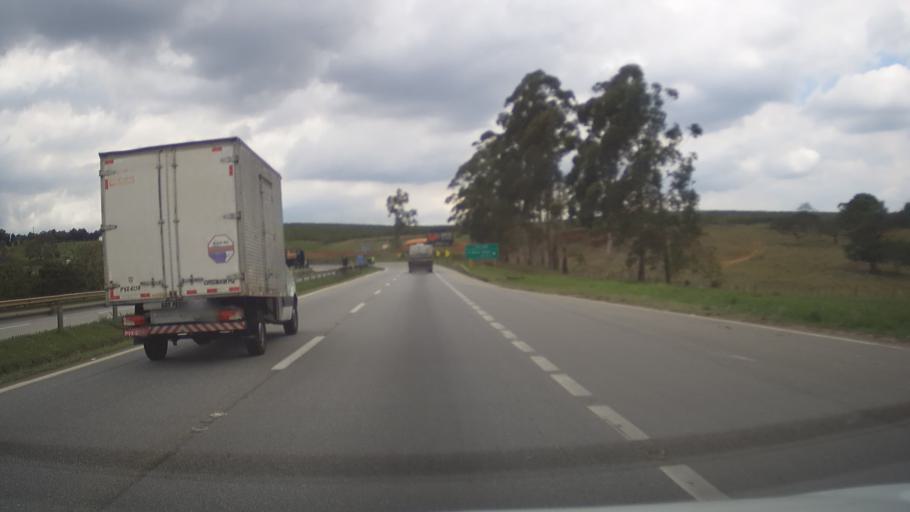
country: BR
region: Minas Gerais
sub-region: Tres Coracoes
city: Tres Coracoes
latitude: -21.4813
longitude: -45.2024
